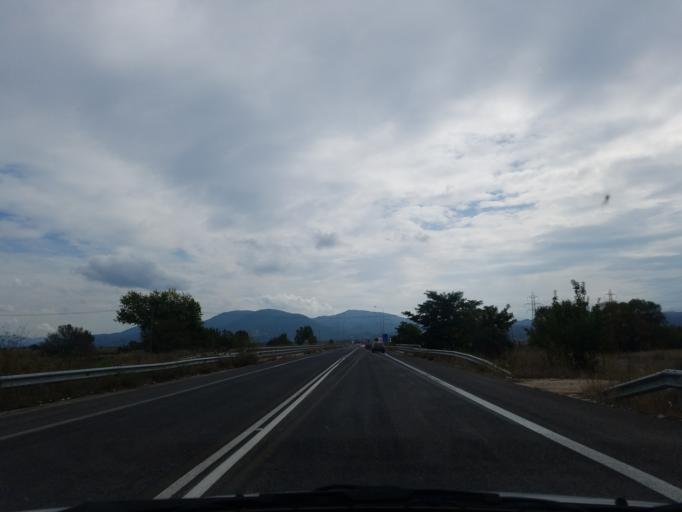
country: GR
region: Central Greece
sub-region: Nomos Fthiotidos
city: Omvriaki
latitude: 39.0572
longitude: 22.3351
